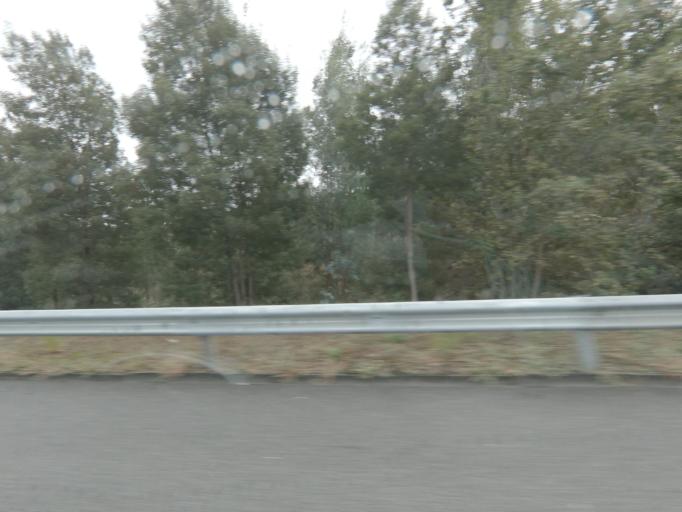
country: PT
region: Porto
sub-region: Paredes
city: Recarei
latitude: 41.1750
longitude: -8.4171
